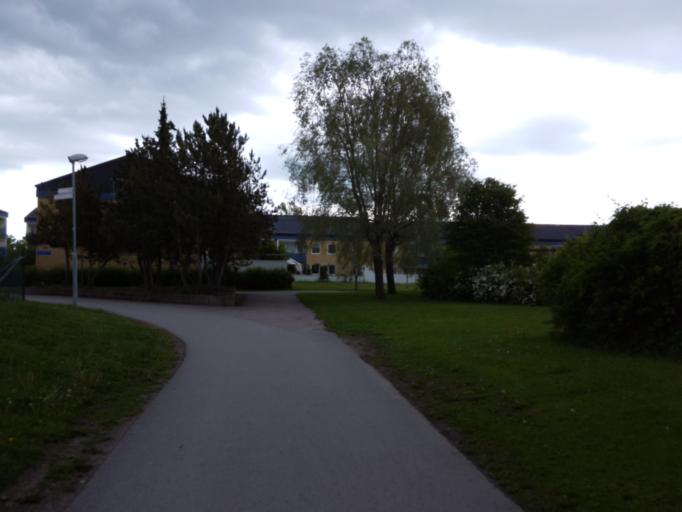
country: SE
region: Uppsala
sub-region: Uppsala Kommun
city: Gamla Uppsala
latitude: 59.8865
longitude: 17.6530
